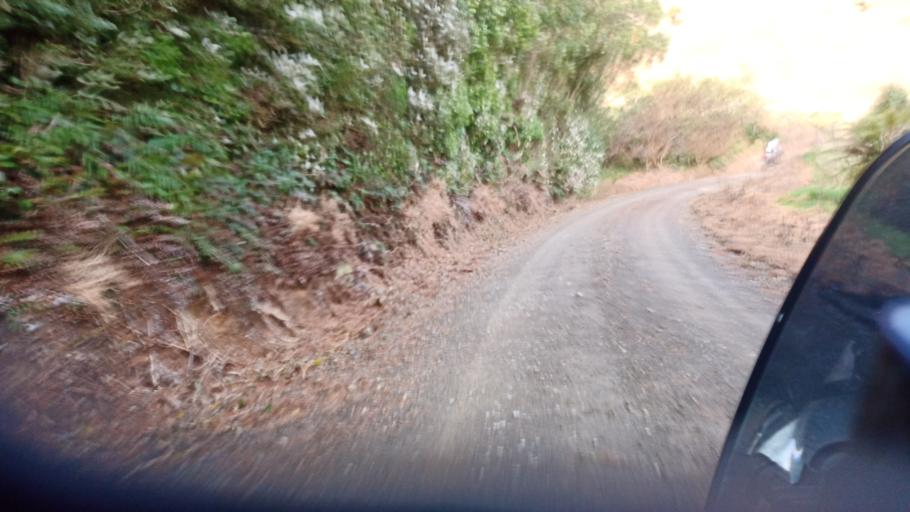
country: NZ
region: Gisborne
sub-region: Gisborne District
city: Gisborne
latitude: -38.4586
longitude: 177.5389
